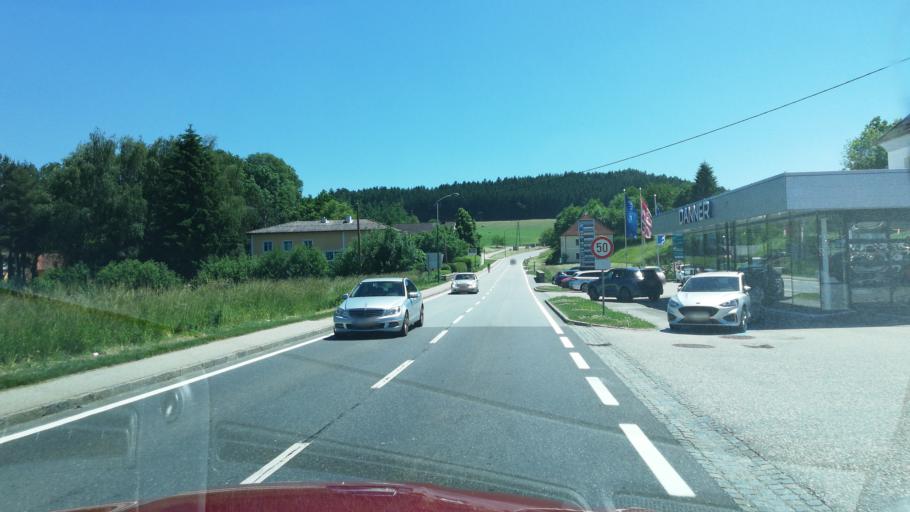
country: AT
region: Upper Austria
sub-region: Politischer Bezirk Vocklabruck
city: Niederthalheim
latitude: 48.1386
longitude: 13.7333
